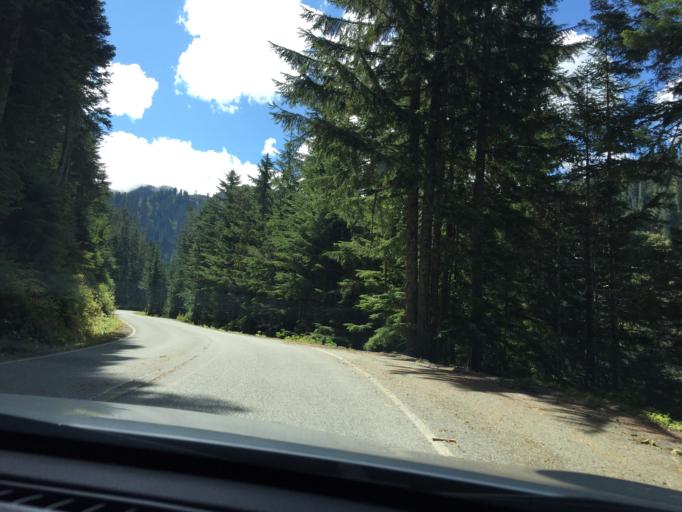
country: CA
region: British Columbia
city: Agassiz
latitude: 48.8651
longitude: -121.6553
